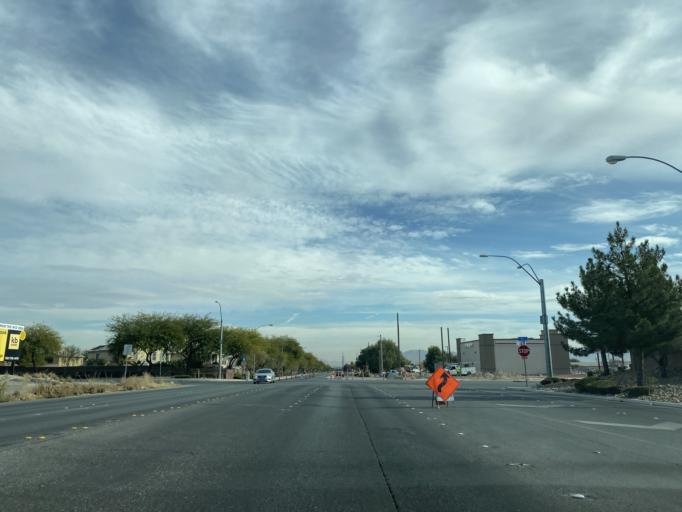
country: US
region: Nevada
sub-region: Clark County
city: North Las Vegas
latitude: 36.2469
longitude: -115.1357
